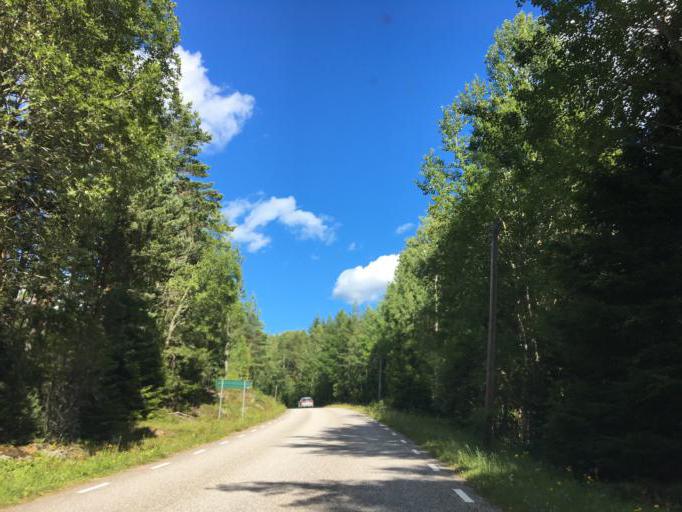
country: SE
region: OErebro
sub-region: Askersunds Kommun
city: Askersund
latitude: 58.8346
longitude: 14.7240
